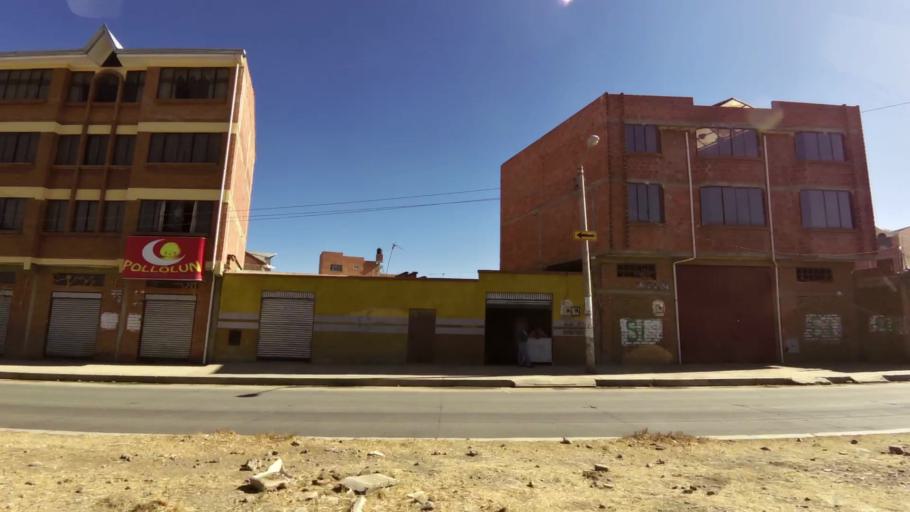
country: BO
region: La Paz
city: La Paz
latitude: -16.5274
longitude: -68.2048
